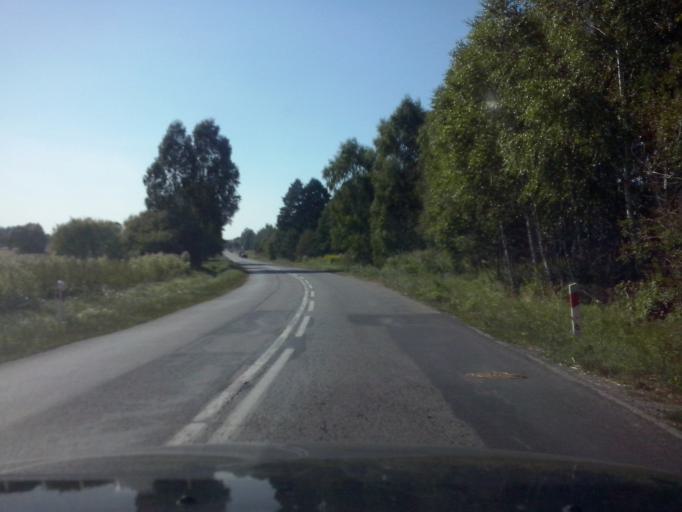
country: PL
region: Swietokrzyskie
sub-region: Powiat kielecki
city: Daleszyce
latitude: 50.8086
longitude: 20.7873
